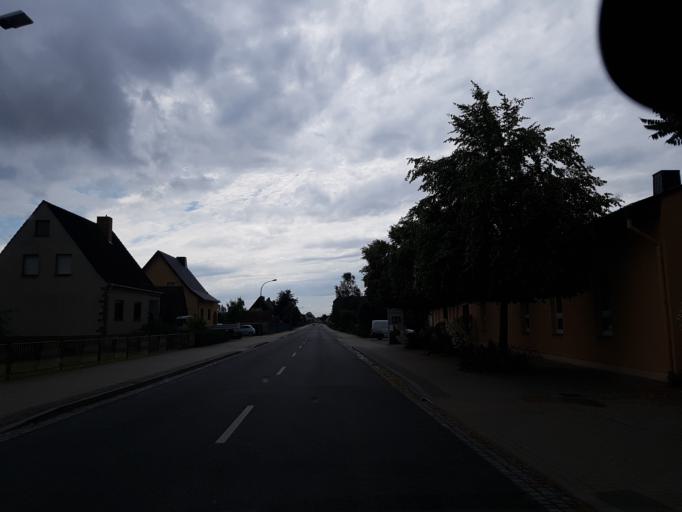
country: DE
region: Saxony-Anhalt
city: Seyda
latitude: 51.8833
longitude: 12.9186
